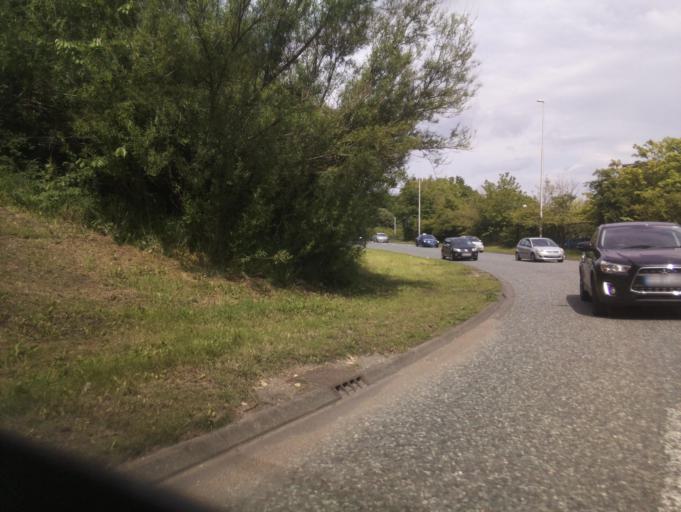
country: GB
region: England
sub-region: Sunderland
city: Washington
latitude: 54.9016
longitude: -1.5378
